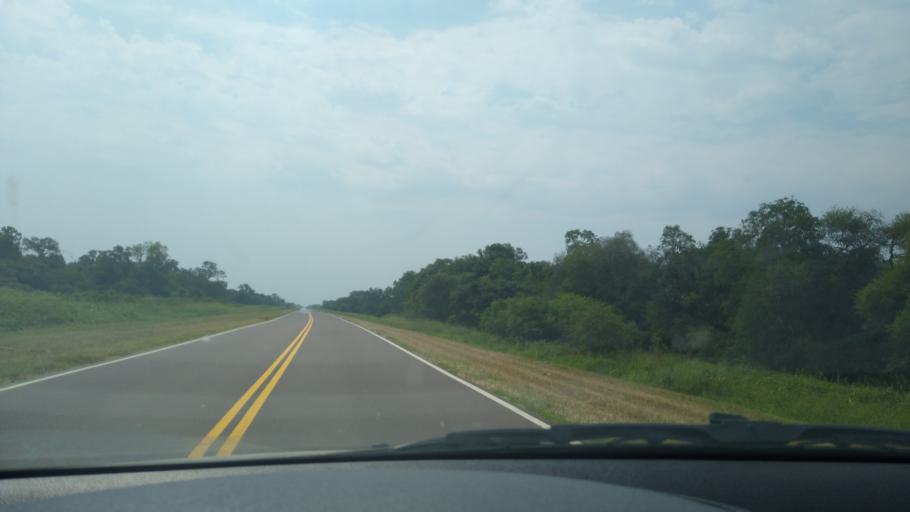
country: AR
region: Chaco
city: Margarita Belen
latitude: -27.0460
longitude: -58.9626
